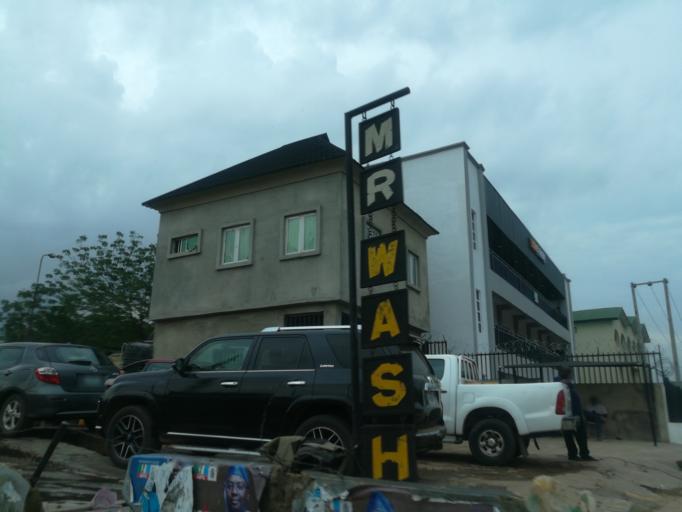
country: NG
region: Oyo
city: Ibadan
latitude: 7.4369
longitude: 3.9076
